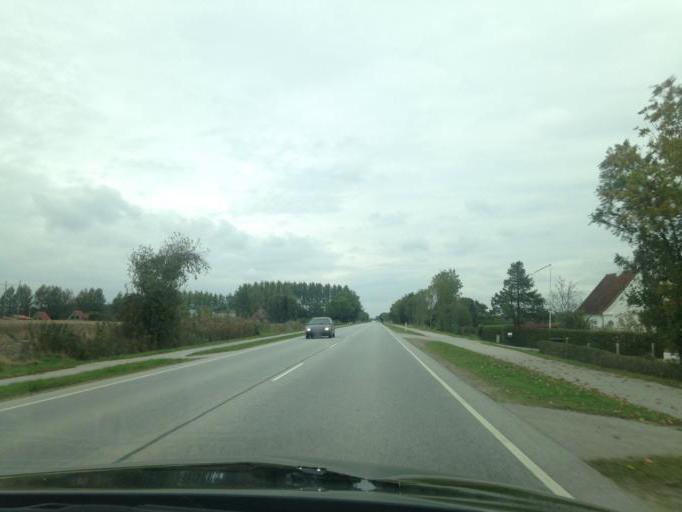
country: DK
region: South Denmark
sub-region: Haderslev Kommune
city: Haderslev
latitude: 55.2879
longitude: 9.4986
